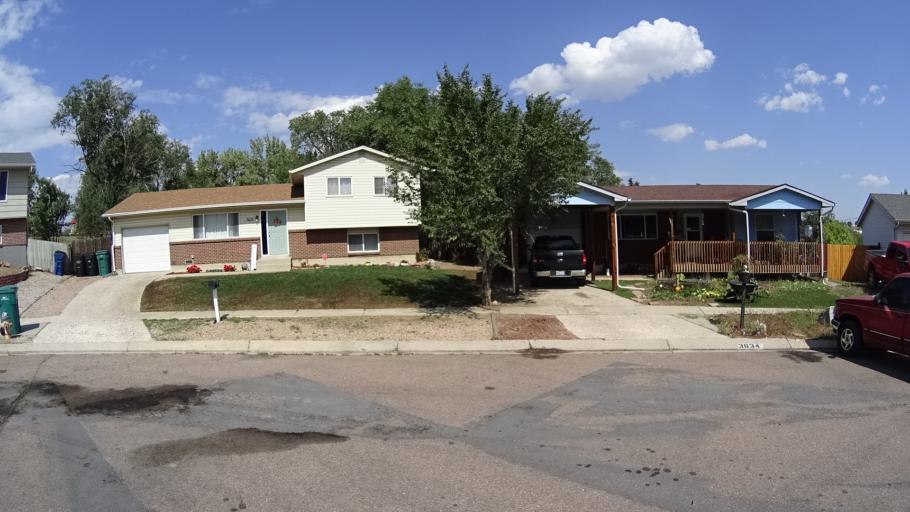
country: US
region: Colorado
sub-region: El Paso County
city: Colorado Springs
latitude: 38.8319
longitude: -104.7641
